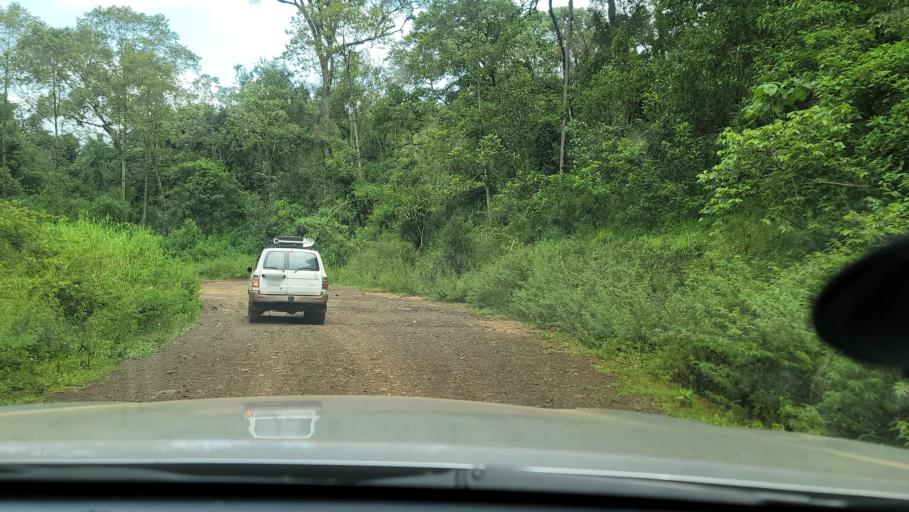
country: ET
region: Southern Nations, Nationalities, and People's Region
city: Bonga
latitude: 7.6486
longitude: 36.2458
